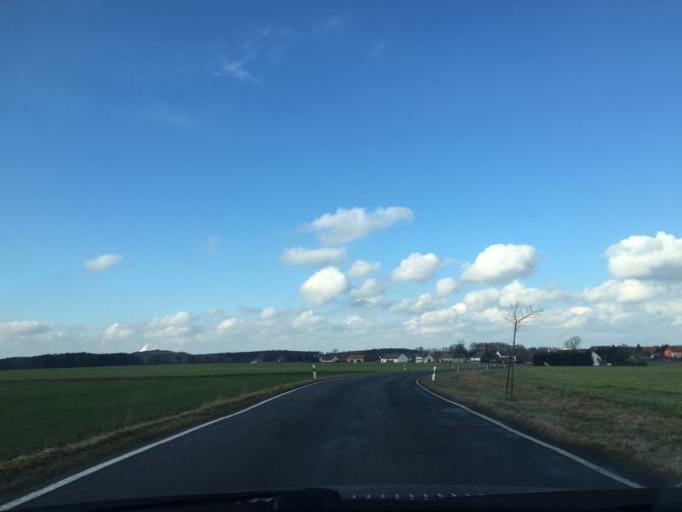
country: DE
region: Saxony
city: Thiendorf
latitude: 51.2736
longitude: 13.7512
